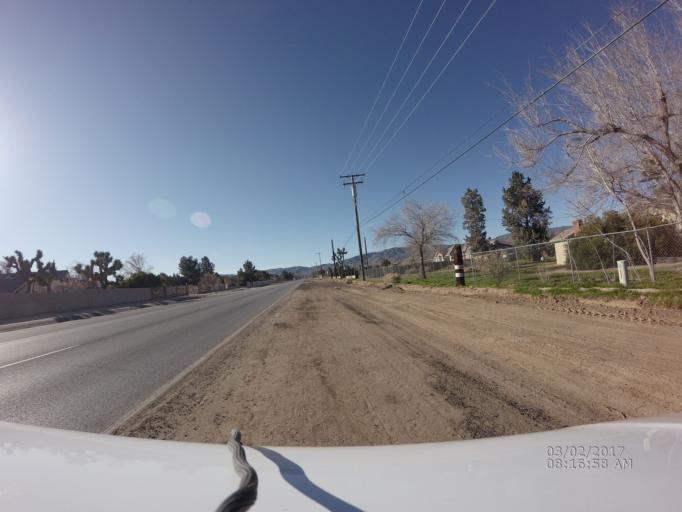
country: US
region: California
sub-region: Los Angeles County
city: Quartz Hill
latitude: 34.6283
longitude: -118.1835
